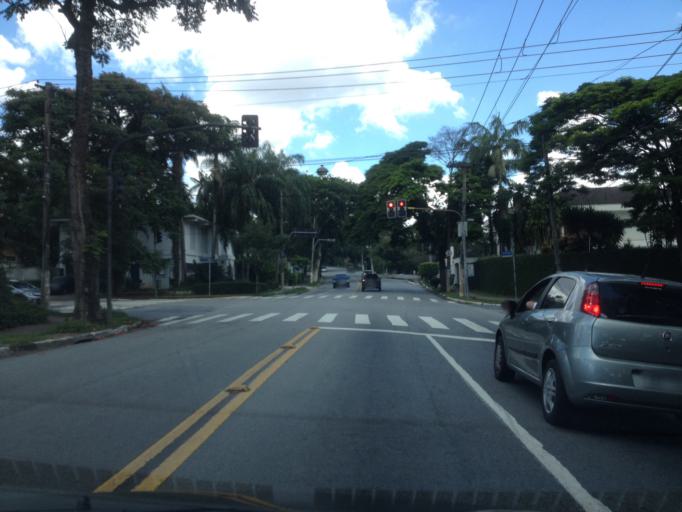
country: BR
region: Sao Paulo
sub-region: Sao Paulo
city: Sao Paulo
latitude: -23.5520
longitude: -46.7058
